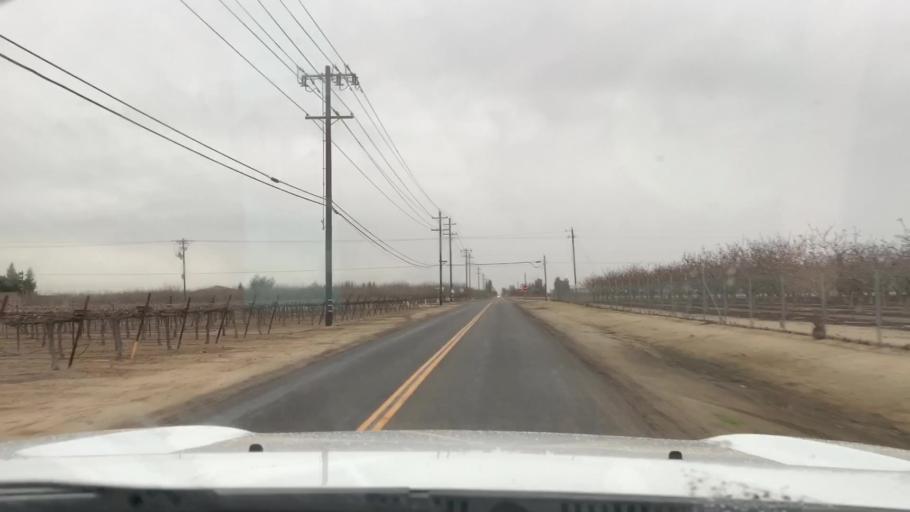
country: US
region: California
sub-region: Kern County
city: Shafter
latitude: 35.5144
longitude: -119.2946
